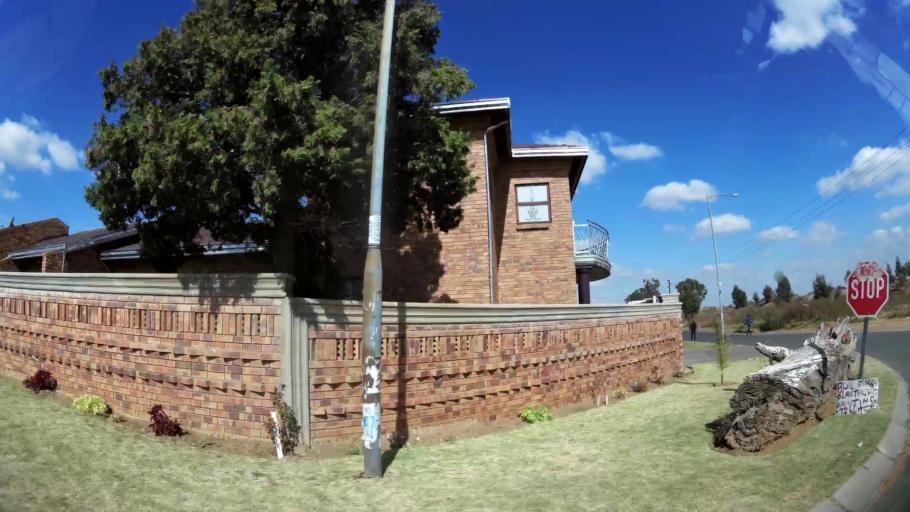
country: ZA
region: Gauteng
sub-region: West Rand District Municipality
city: Krugersdorp
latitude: -26.1485
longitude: 27.7848
